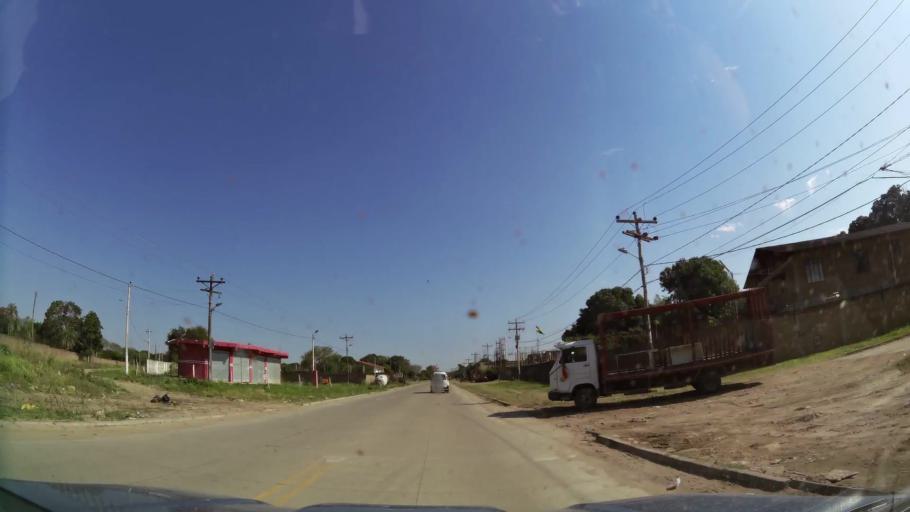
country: BO
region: Santa Cruz
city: Santa Cruz de la Sierra
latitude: -17.7603
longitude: -63.1096
